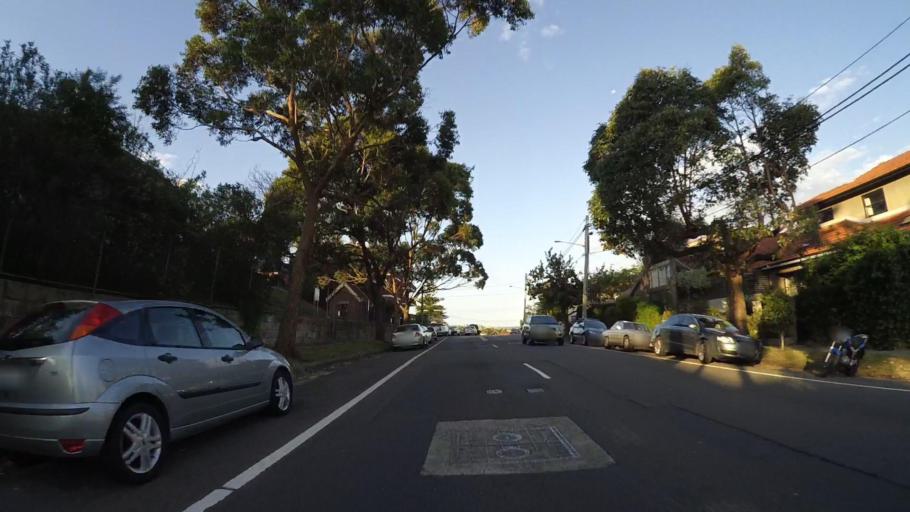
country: AU
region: New South Wales
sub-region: Randwick
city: Randwick
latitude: -33.9223
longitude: 151.2461
